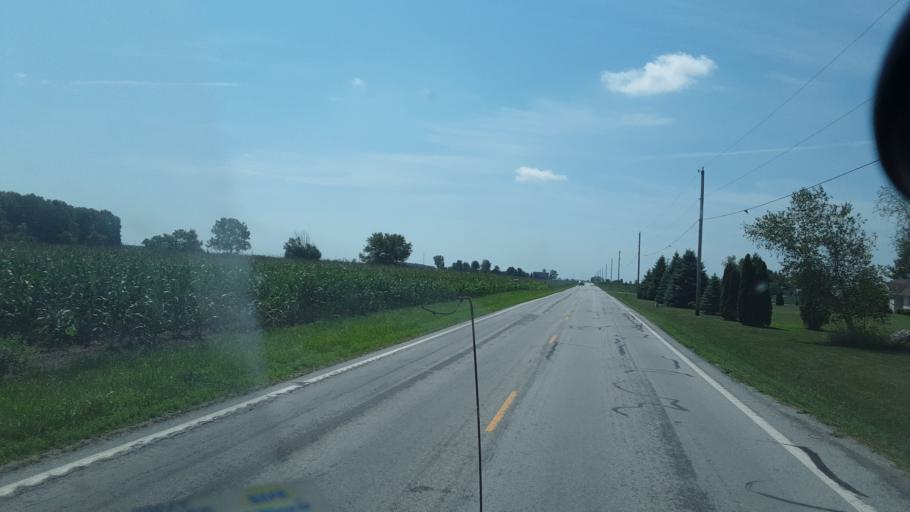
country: US
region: Ohio
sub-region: Hancock County
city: Arlington
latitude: 40.9515
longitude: -83.5749
